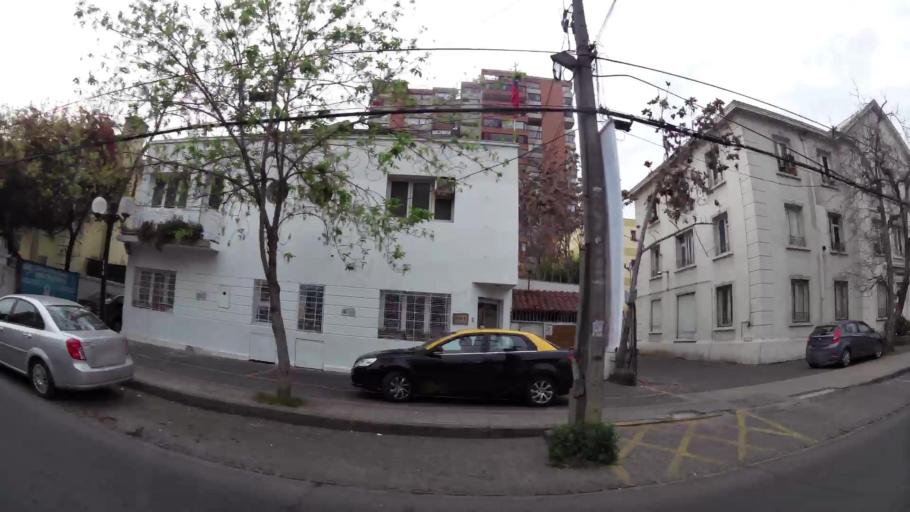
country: CL
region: Santiago Metropolitan
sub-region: Provincia de Santiago
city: Villa Presidente Frei, Nunoa, Santiago, Chile
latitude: -33.4305
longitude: -70.6052
